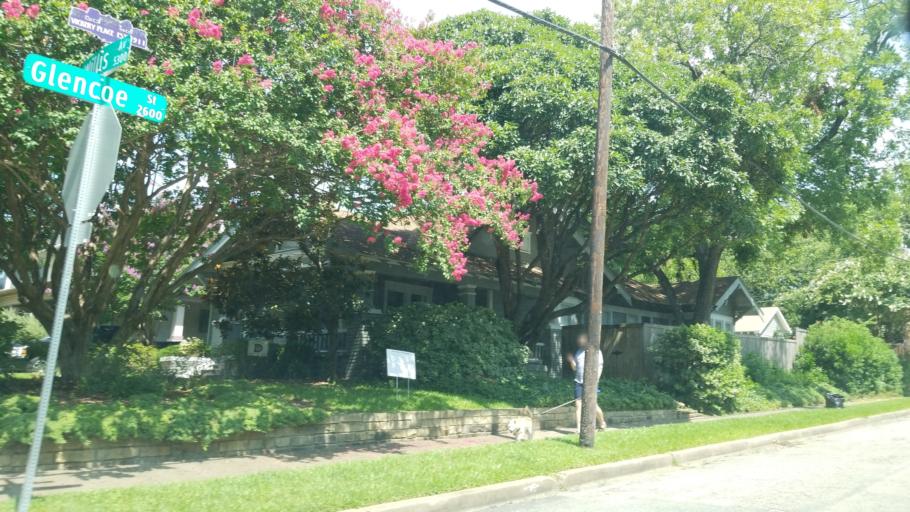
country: US
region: Texas
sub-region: Dallas County
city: Highland Park
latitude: 32.8203
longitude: -96.7774
